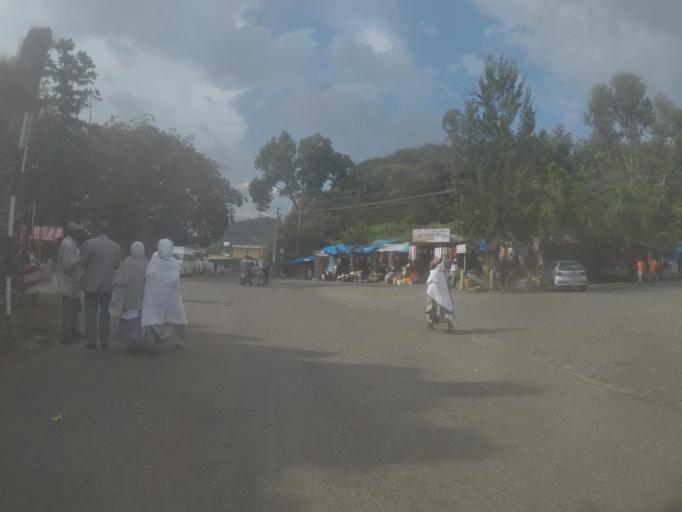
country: ET
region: Amhara
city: Gondar
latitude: 12.6096
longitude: 37.4709
